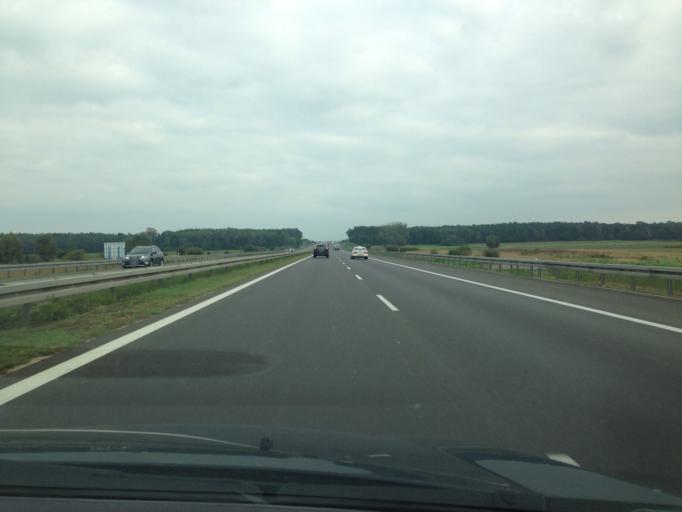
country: PL
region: Greater Poland Voivodeship
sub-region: Powiat poznanski
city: Swarzedz
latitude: 52.3407
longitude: 17.0359
